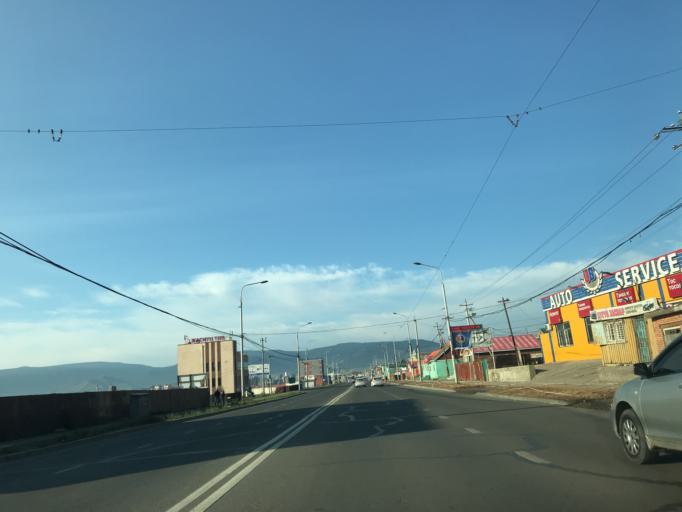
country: MN
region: Ulaanbaatar
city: Ulaanbaatar
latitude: 47.9601
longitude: 106.9166
